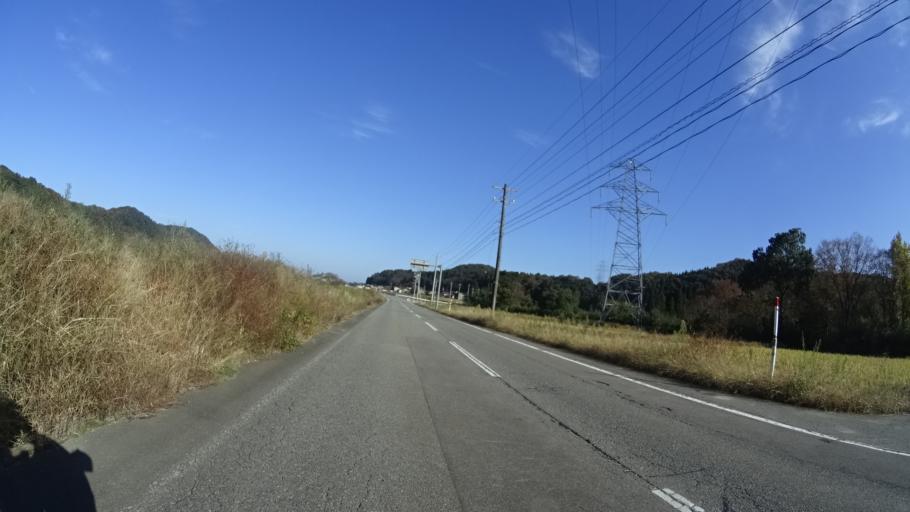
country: JP
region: Ishikawa
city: Komatsu
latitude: 36.2646
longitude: 136.3936
